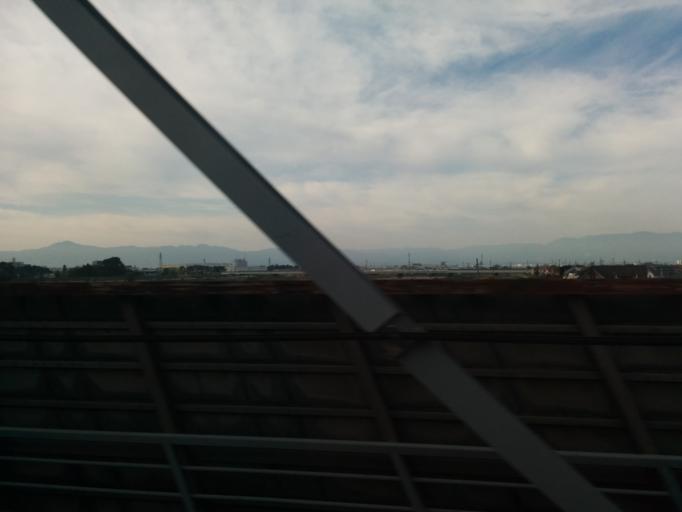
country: JP
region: Shiga Prefecture
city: Moriyama
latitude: 35.0549
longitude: 136.0154
